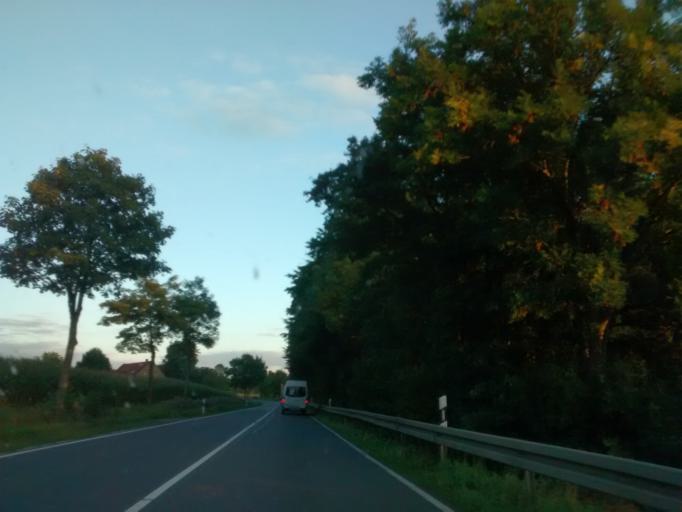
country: DE
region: North Rhine-Westphalia
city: Borgholzhausen
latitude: 52.0813
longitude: 8.2904
